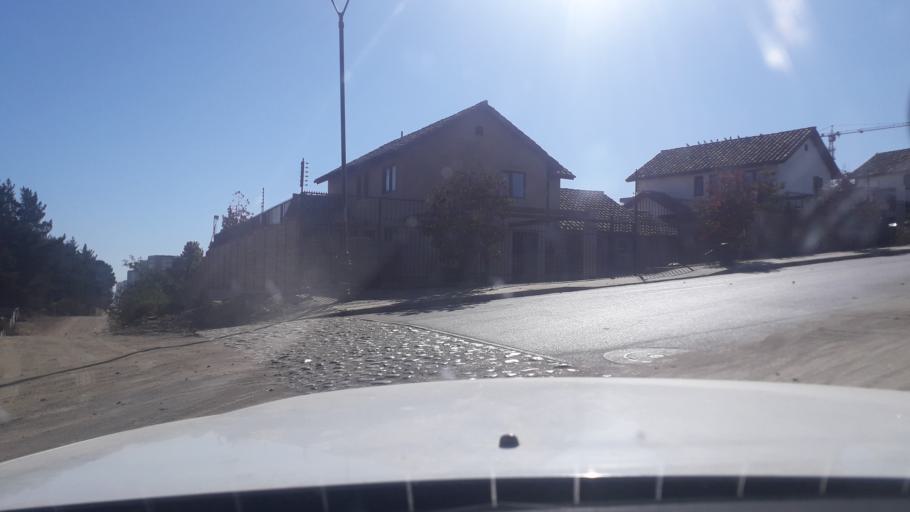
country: CL
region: Valparaiso
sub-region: Provincia de Valparaiso
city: Vina del Mar
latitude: -32.9526
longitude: -71.5339
